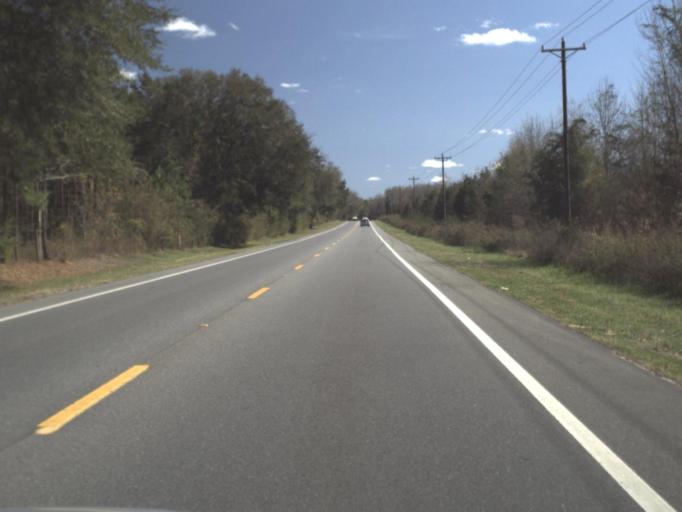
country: US
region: Florida
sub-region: Gadsden County
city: Gretna
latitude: 30.6008
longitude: -84.6516
